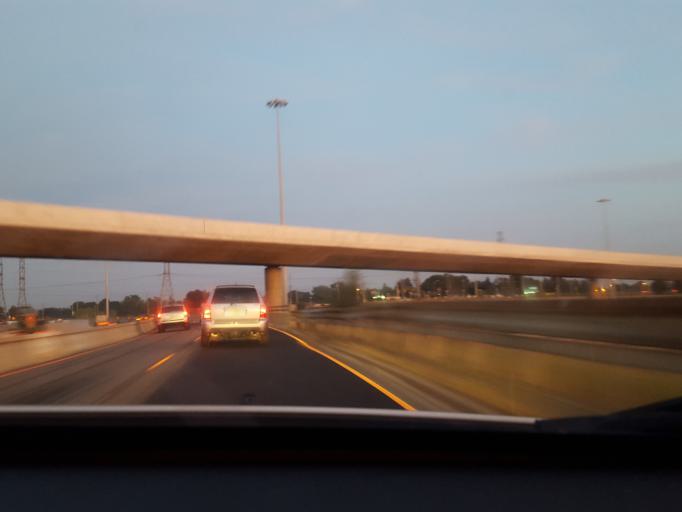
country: CA
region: Ontario
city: Etobicoke
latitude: 43.6709
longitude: -79.5891
